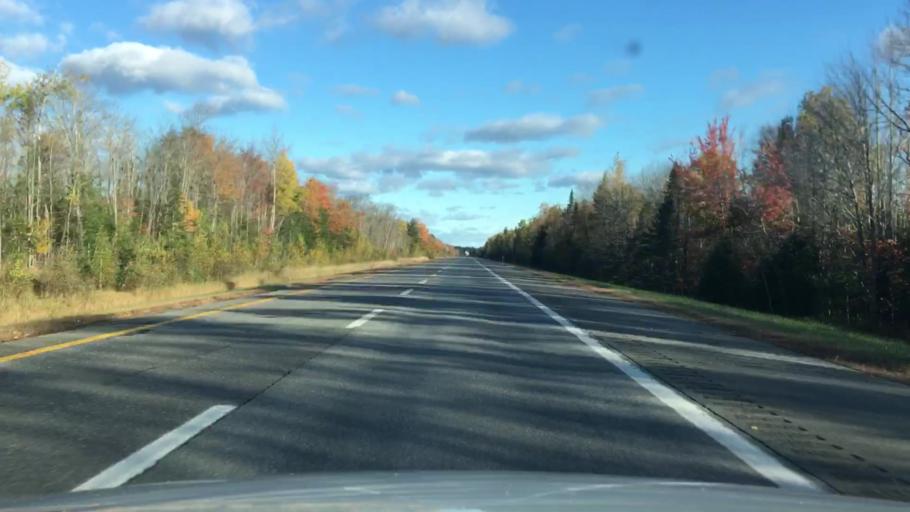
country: US
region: Maine
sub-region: Penobscot County
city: Greenbush
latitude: 45.0833
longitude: -68.6927
